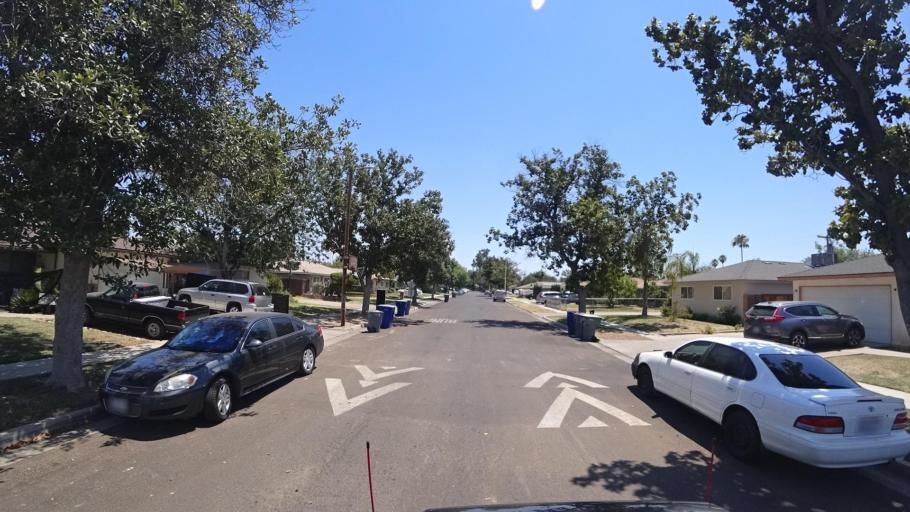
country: US
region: California
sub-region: Fresno County
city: Sunnyside
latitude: 36.7621
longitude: -119.7254
